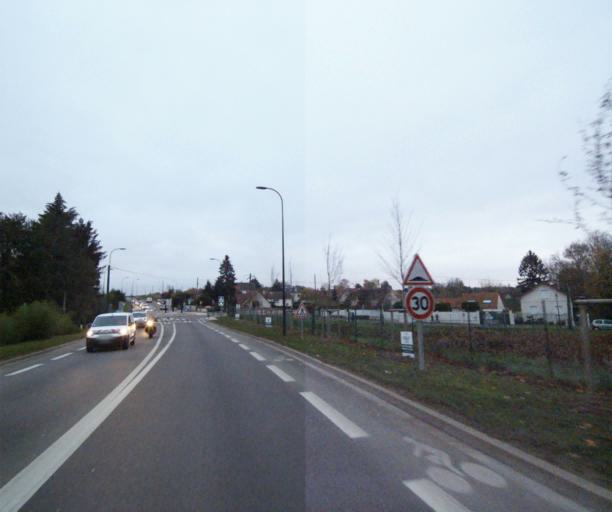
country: FR
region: Ile-de-France
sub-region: Departement des Yvelines
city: Villennes-sur-Seine
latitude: 48.9399
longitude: 1.9776
